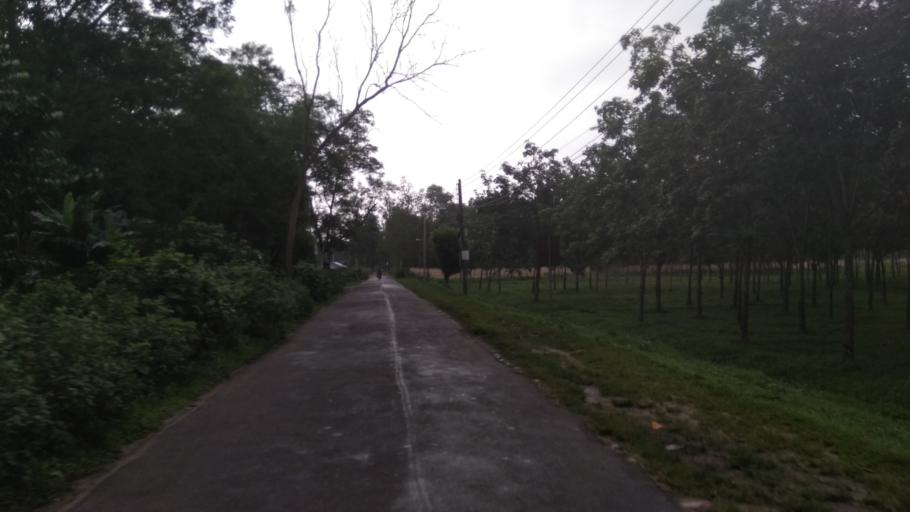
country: IN
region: Tripura
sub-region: Dhalai
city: Kamalpur
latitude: 24.3008
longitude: 91.7356
